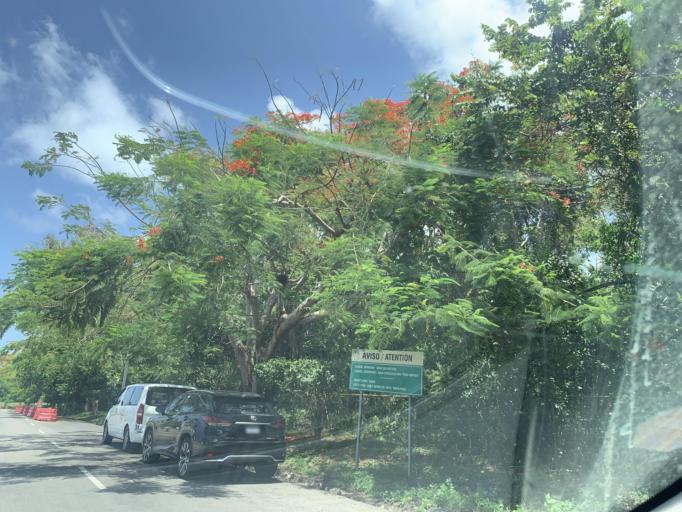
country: DO
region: Puerto Plata
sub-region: Puerto Plata
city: Puerto Plata
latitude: 19.7539
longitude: -70.5628
